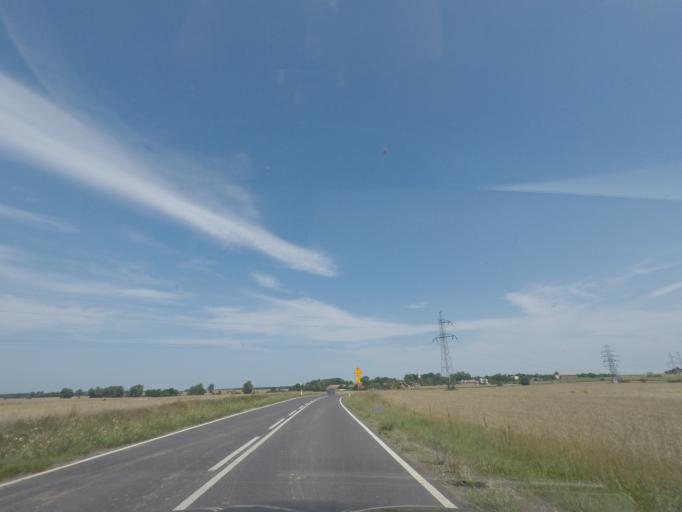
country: PL
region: West Pomeranian Voivodeship
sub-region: Powiat koszalinski
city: Sianow
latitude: 54.2880
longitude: 16.2721
